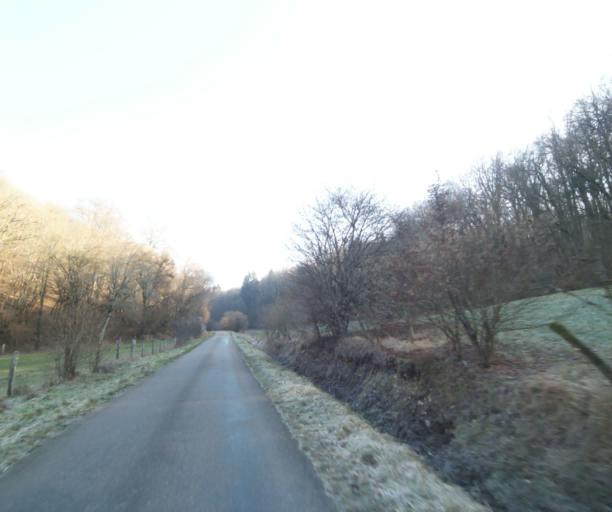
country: FR
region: Champagne-Ardenne
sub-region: Departement de la Haute-Marne
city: Joinville
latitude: 48.4902
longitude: 5.2257
